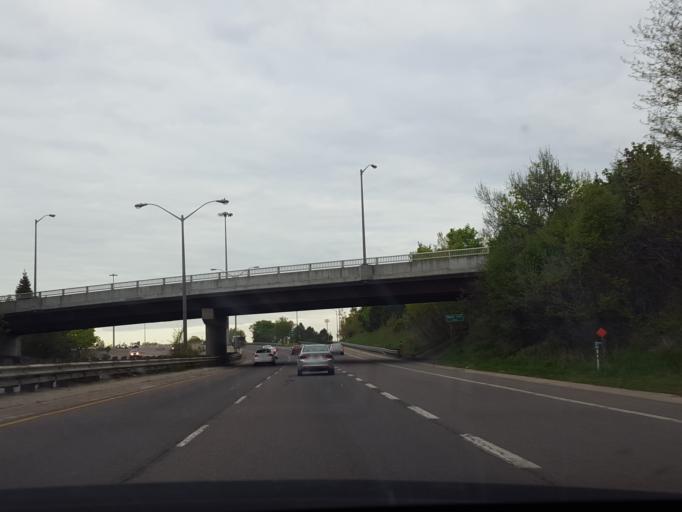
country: CA
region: Ontario
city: Toronto
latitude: 43.7094
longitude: -79.5004
